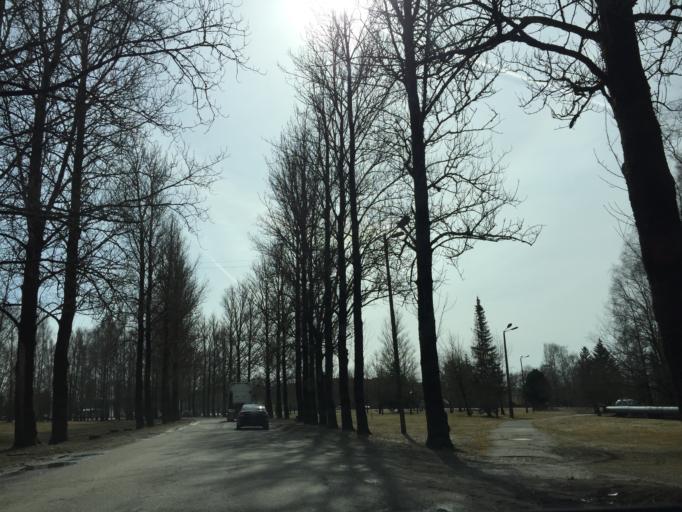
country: EE
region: Paernumaa
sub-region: Paernu linn
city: Parnu
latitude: 58.3759
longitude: 24.5406
